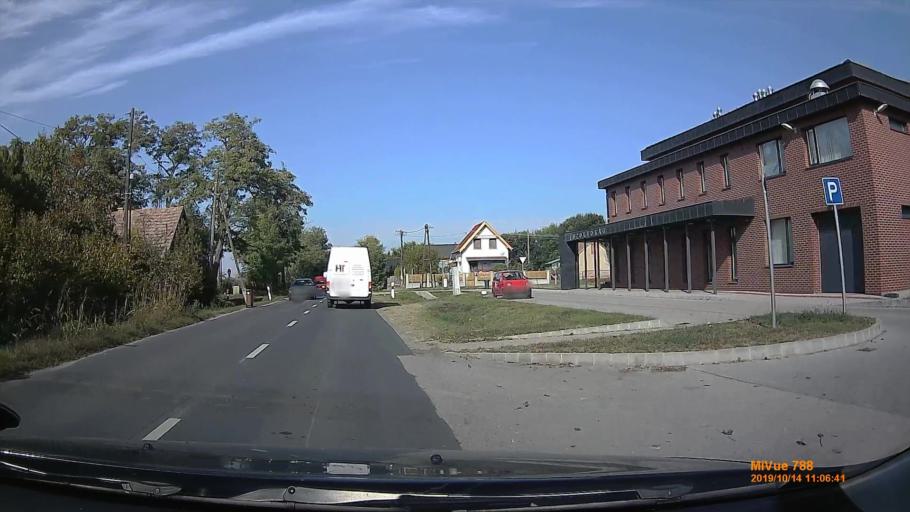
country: HU
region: Pest
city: Monor
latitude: 47.3615
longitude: 19.4329
